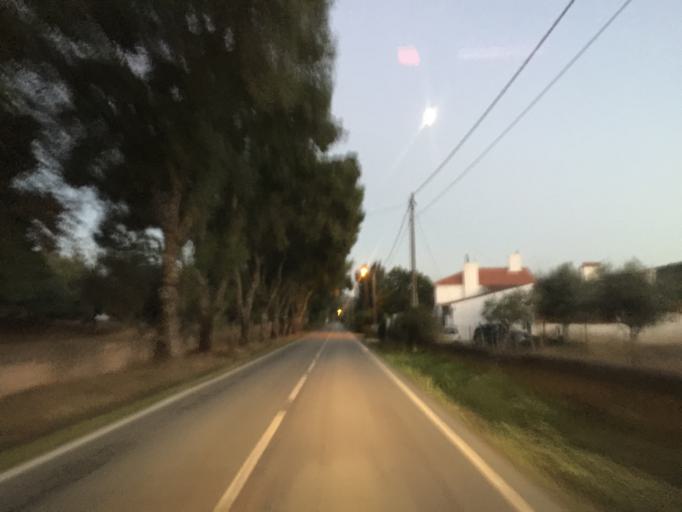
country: PT
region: Portalegre
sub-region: Marvao
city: Marvao
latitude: 39.3930
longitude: -7.4159
